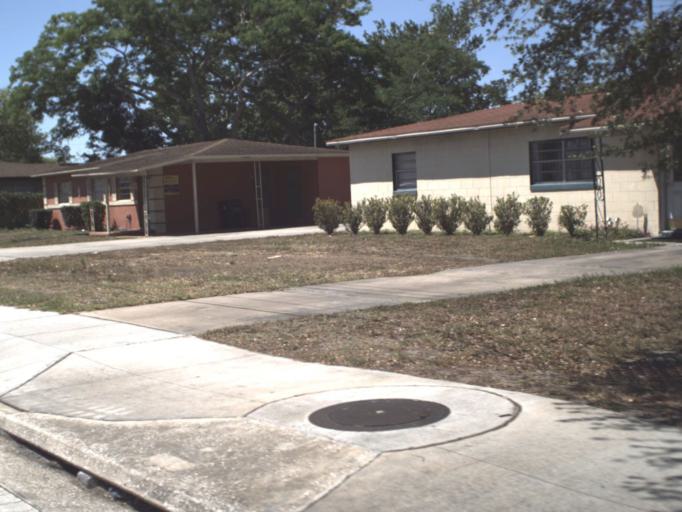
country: US
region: Florida
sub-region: Orange County
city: Azalea Park
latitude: 28.5263
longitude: -81.3105
